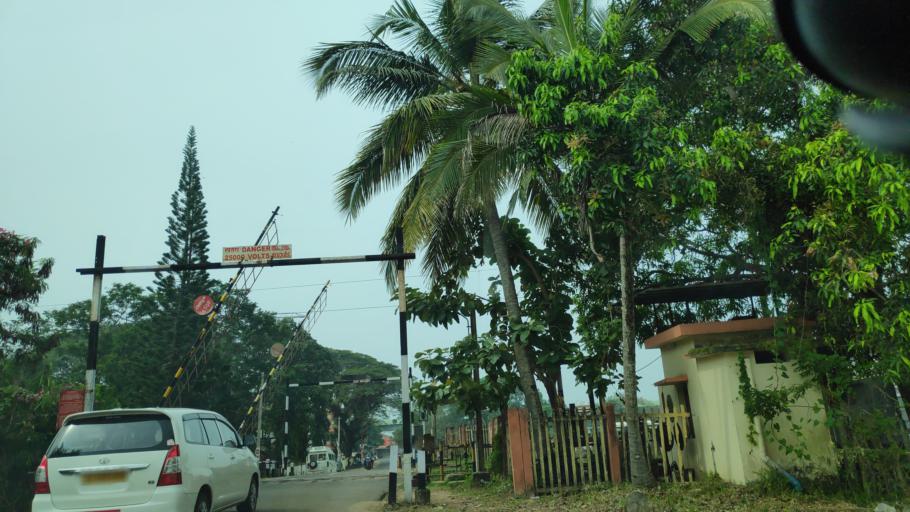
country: IN
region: Kerala
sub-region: Alappuzha
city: Alleppey
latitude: 9.4940
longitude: 76.3204
